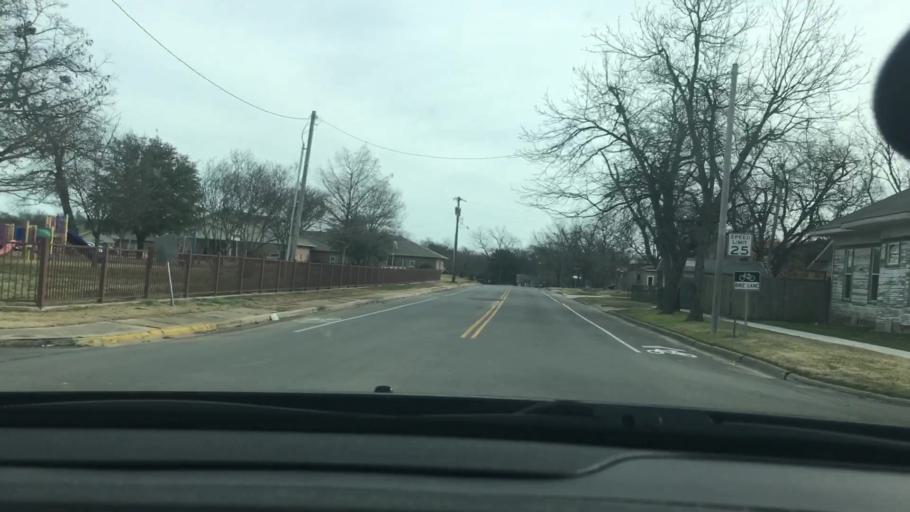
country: US
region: Oklahoma
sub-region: Carter County
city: Ardmore
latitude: 34.1766
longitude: -97.1202
